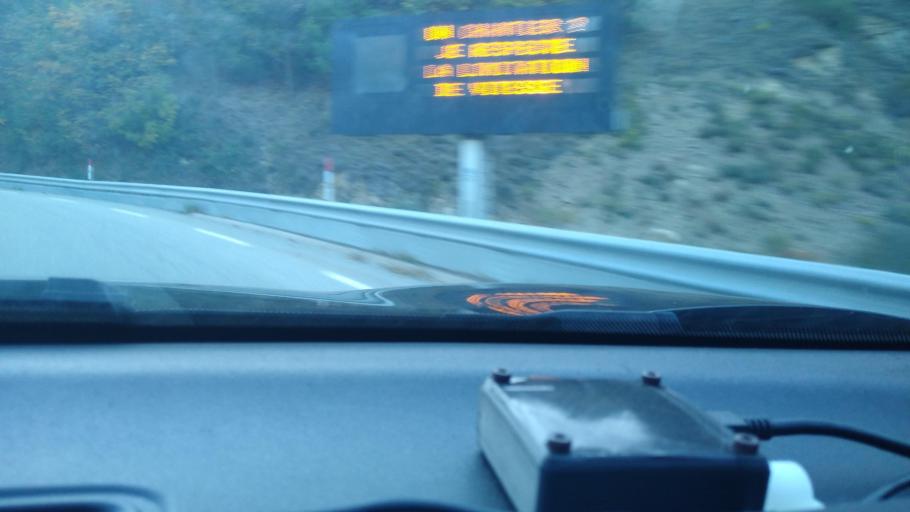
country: FR
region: Languedoc-Roussillon
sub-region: Departement des Pyrenees-Orientales
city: Vernet-les-Bains
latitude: 42.5170
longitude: 2.1959
